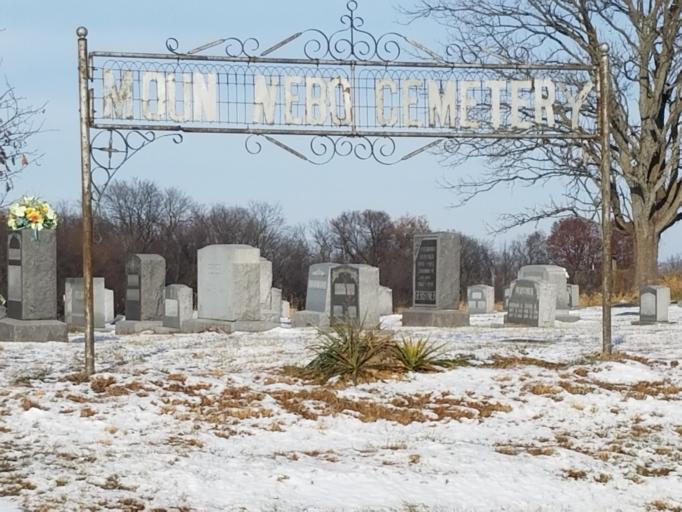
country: US
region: Missouri
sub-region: Carroll County
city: Carrollton
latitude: 39.2028
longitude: -93.4675
